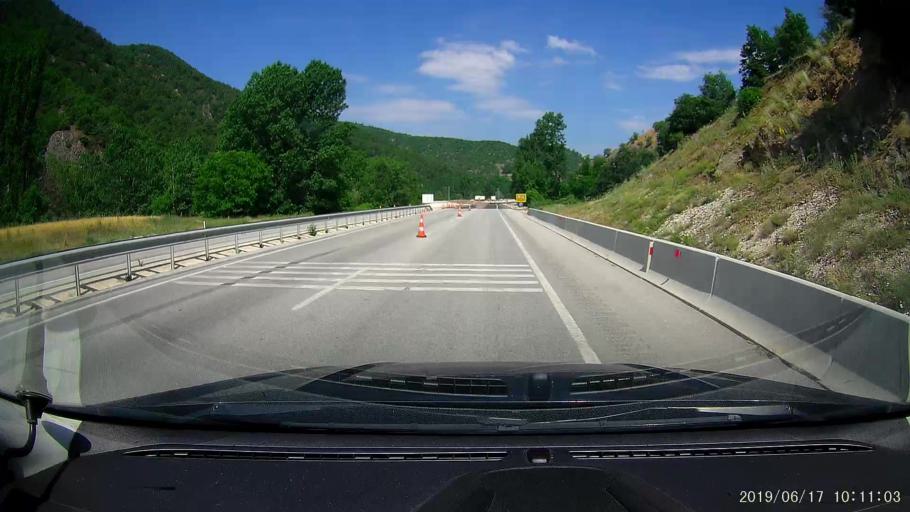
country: TR
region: Amasya
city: Saraycik
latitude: 40.9671
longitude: 35.0893
